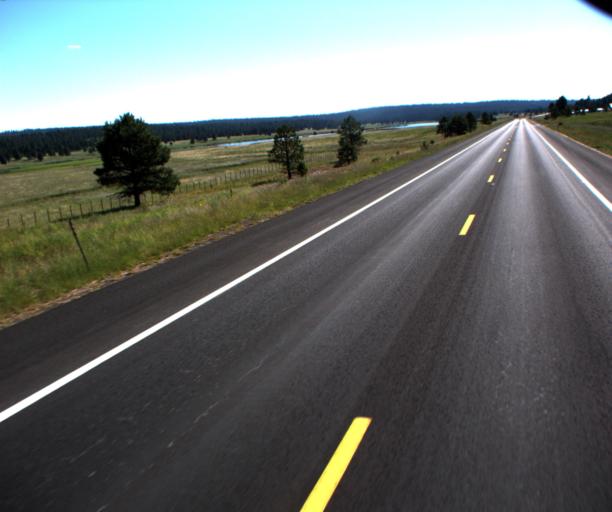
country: US
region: Arizona
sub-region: Apache County
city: Eagar
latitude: 33.8274
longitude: -109.1054
